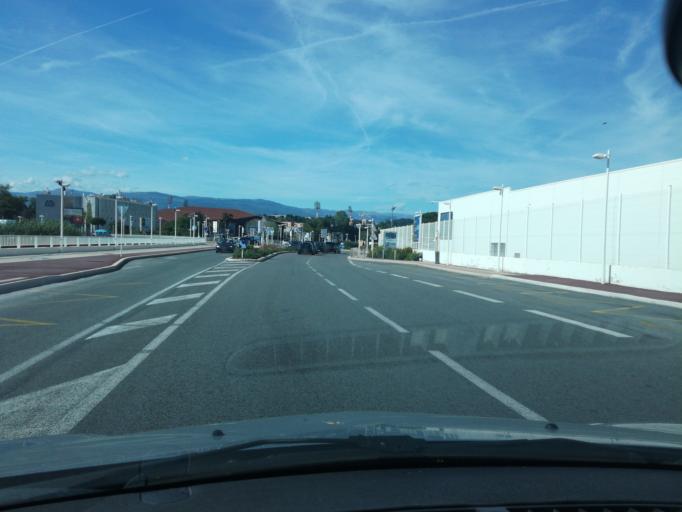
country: FR
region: Provence-Alpes-Cote d'Azur
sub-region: Departement des Alpes-Maritimes
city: Mandelieu-la-Napoule
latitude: 43.5490
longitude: 6.9622
